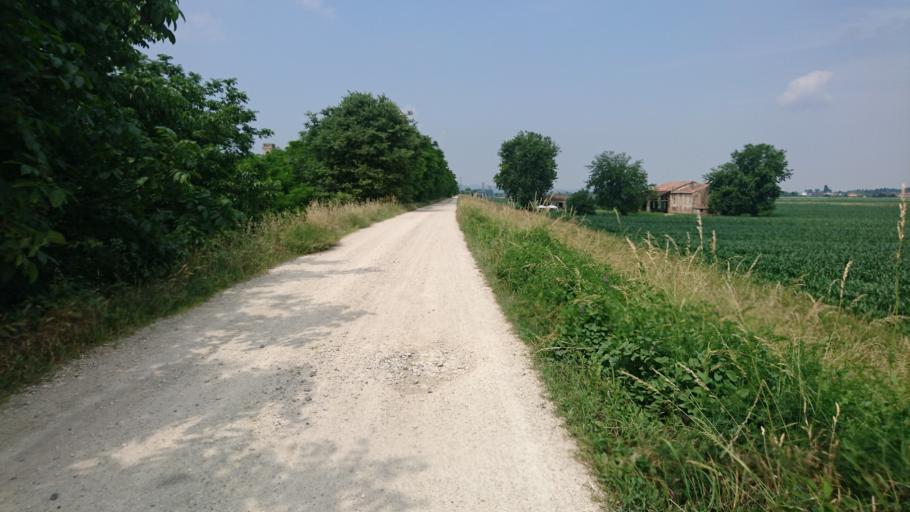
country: IT
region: Veneto
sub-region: Provincia di Padova
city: Bovolenta
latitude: 45.2770
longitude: 11.9070
